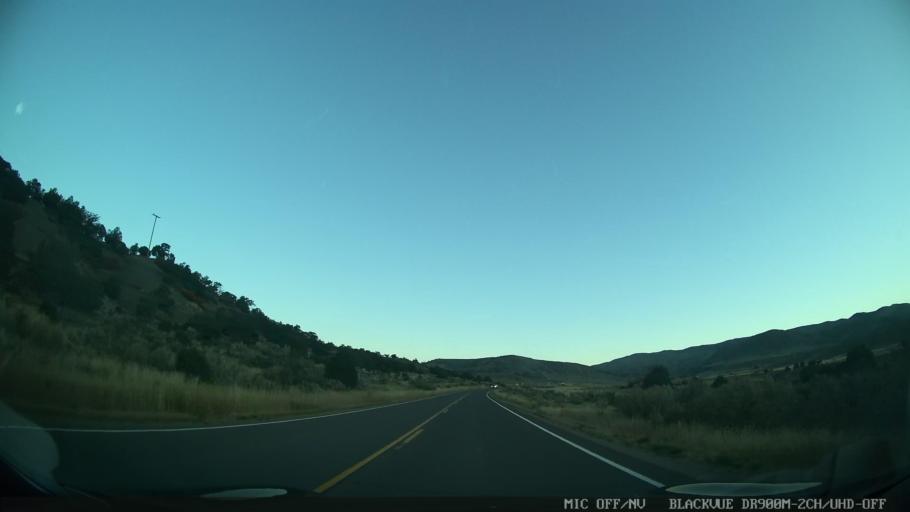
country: US
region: Colorado
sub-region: Eagle County
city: Edwards
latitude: 39.7331
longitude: -106.6791
